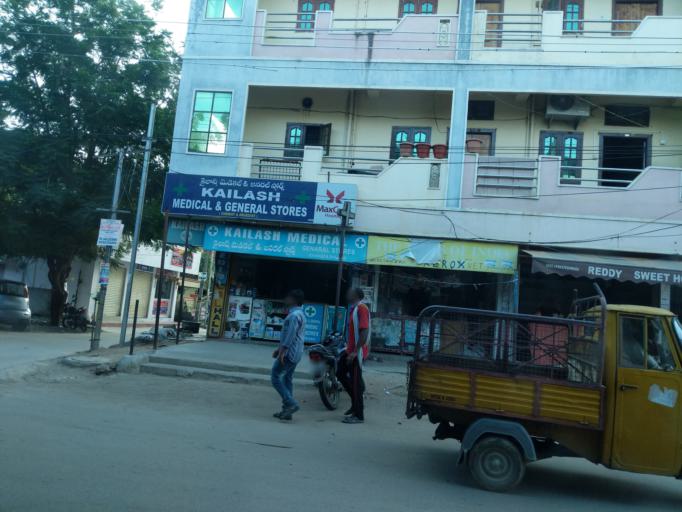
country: IN
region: Telangana
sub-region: Medak
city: Serilingampalle
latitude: 17.4931
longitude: 78.3278
